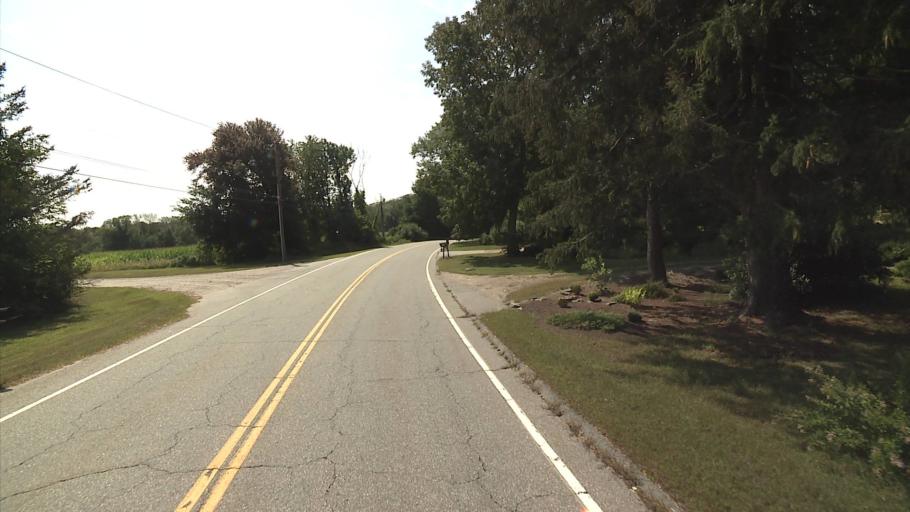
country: US
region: Connecticut
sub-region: Windham County
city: Plainfield Village
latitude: 41.6820
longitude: -71.9665
